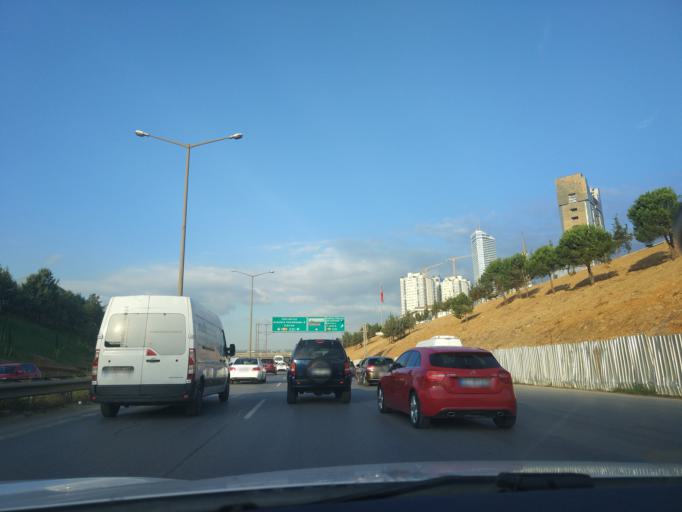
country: TR
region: Istanbul
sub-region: Atasehir
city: Atasehir
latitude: 40.9892
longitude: 29.1101
